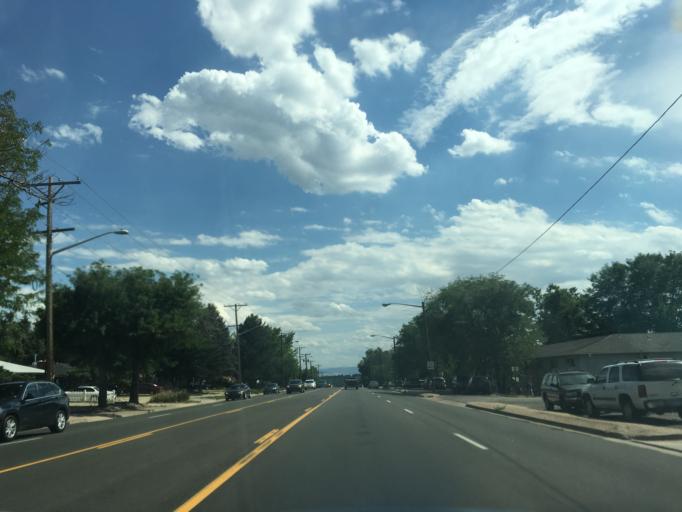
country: US
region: Colorado
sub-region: Arapahoe County
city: Sheridan
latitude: 39.6716
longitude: -105.0533
